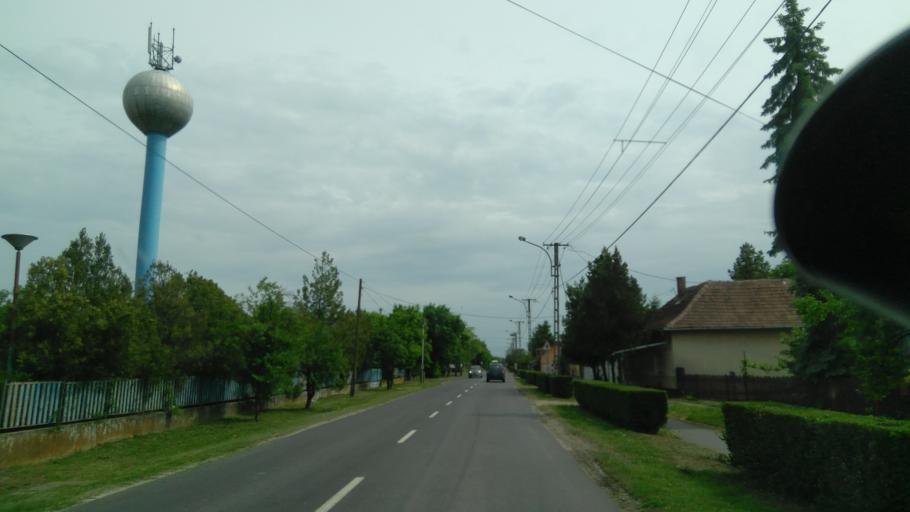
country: HU
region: Bekes
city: Sarkad
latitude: 46.8056
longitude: 21.3820
